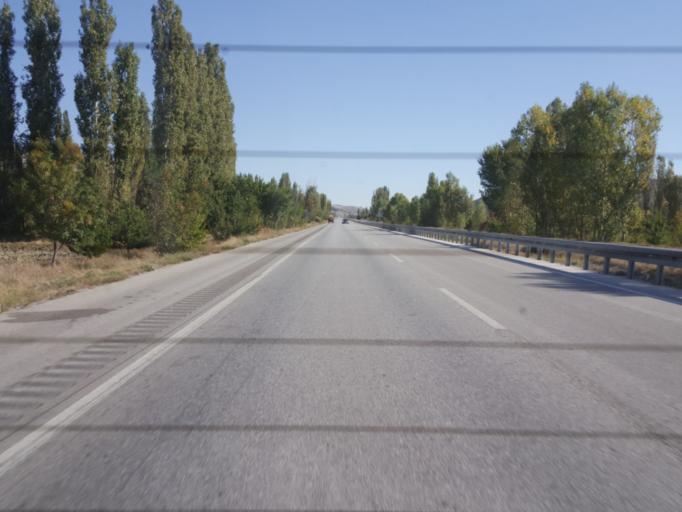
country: TR
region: Corum
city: Sungurlu
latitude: 40.1861
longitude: 34.4948
